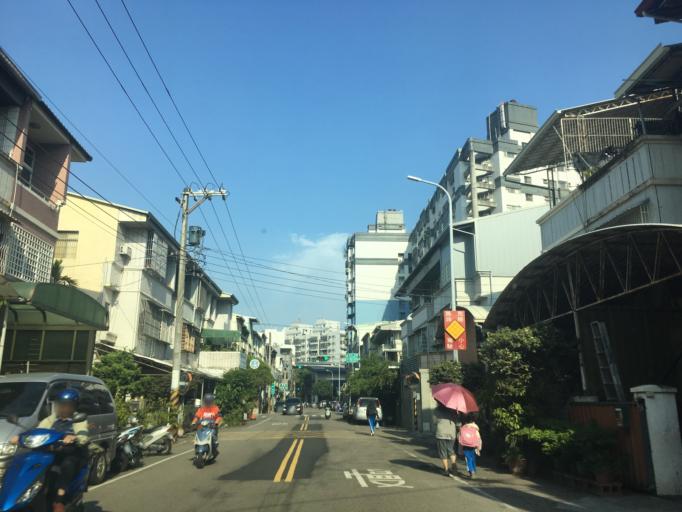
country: TW
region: Taiwan
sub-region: Taichung City
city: Taichung
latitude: 24.1815
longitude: 120.6929
